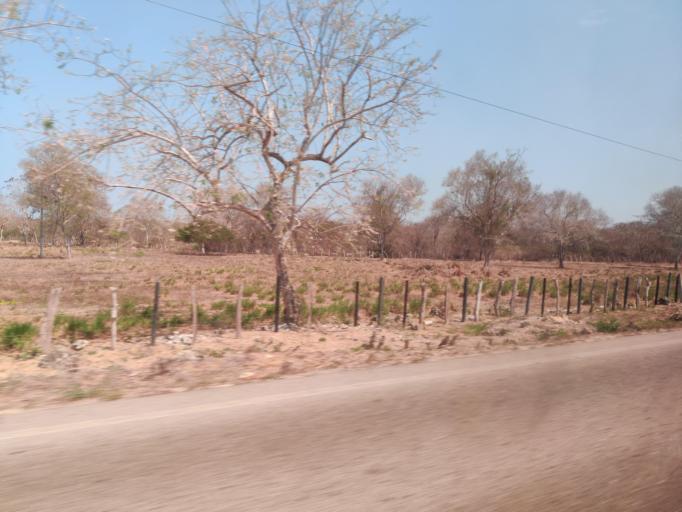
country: CO
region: Bolivar
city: Turbana
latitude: 10.2125
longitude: -75.6006
